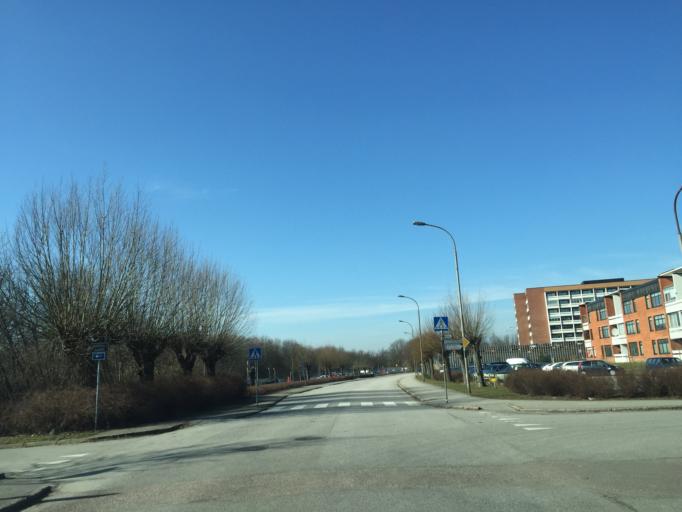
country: SE
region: Skane
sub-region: Lunds Kommun
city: Lund
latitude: 55.6904
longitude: 13.1744
